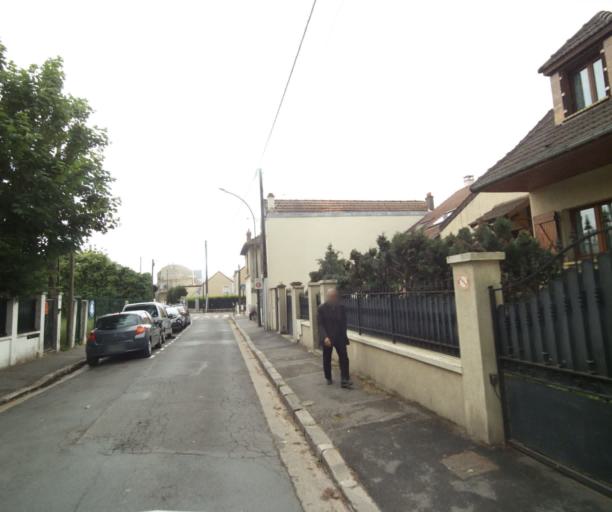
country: FR
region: Ile-de-France
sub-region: Departement du Val-d'Oise
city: Bezons
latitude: 48.9424
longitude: 2.2252
